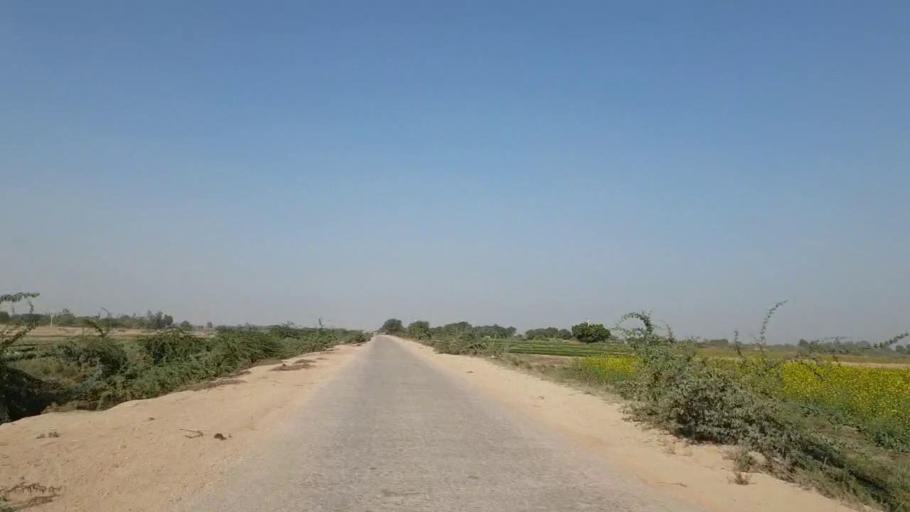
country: PK
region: Sindh
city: Digri
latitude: 25.0181
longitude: 69.1058
